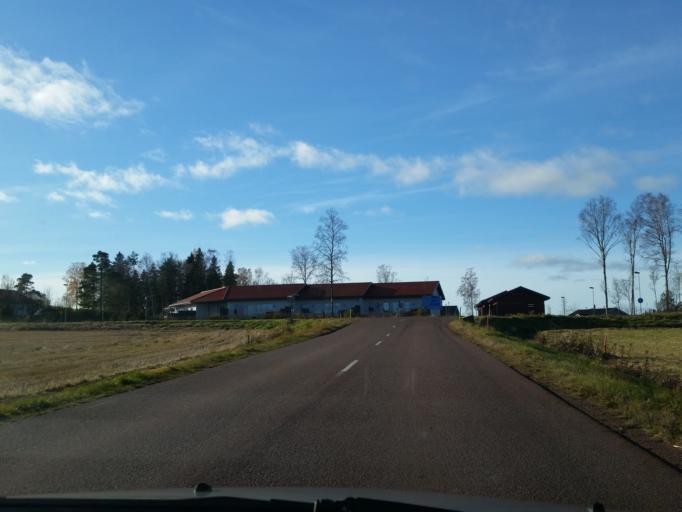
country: AX
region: Alands landsbygd
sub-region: Jomala
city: Jomala
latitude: 60.1851
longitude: 19.9529
